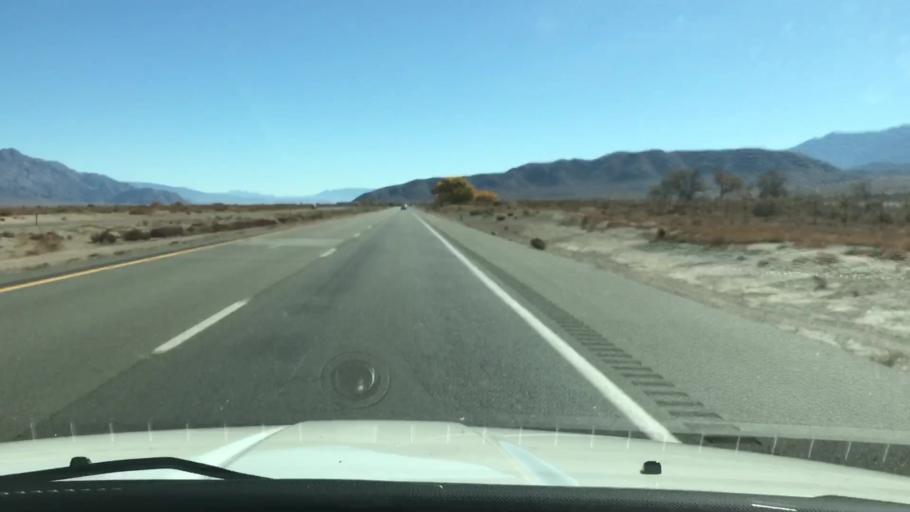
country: US
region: California
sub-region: Inyo County
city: Lone Pine
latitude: 36.7254
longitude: -118.1427
